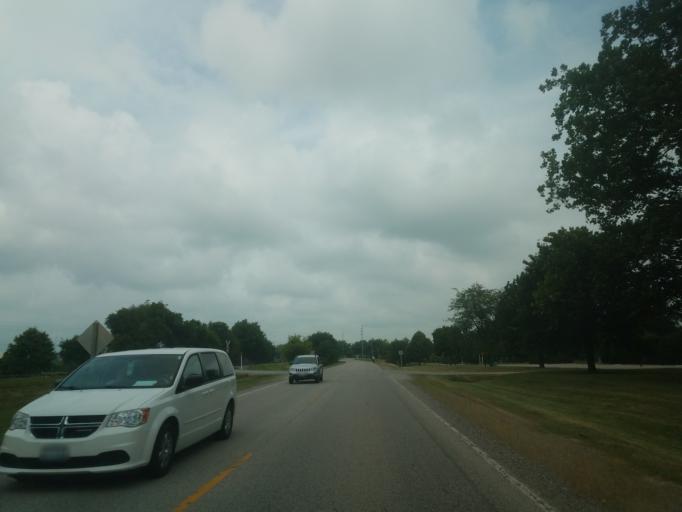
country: US
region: Illinois
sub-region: McLean County
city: Bloomington
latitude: 40.4861
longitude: -89.0151
